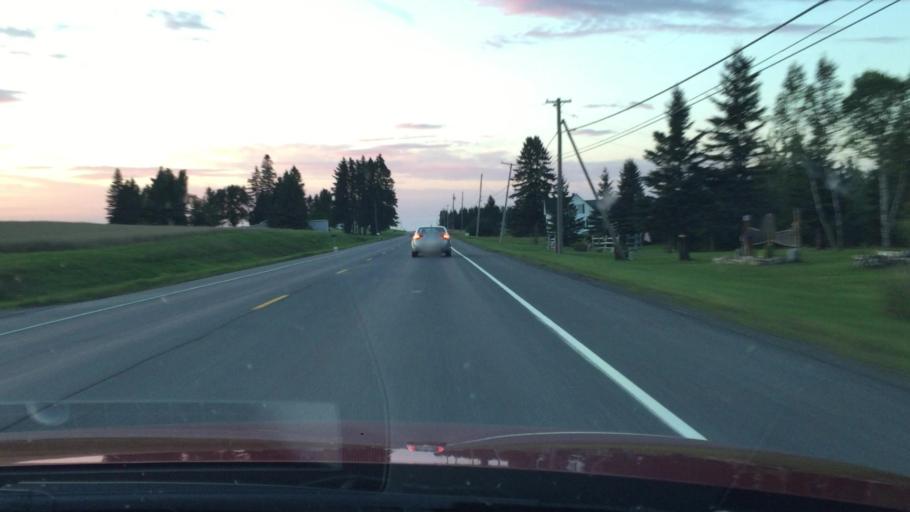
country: US
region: Maine
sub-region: Aroostook County
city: Easton
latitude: 46.5868
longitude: -67.9608
